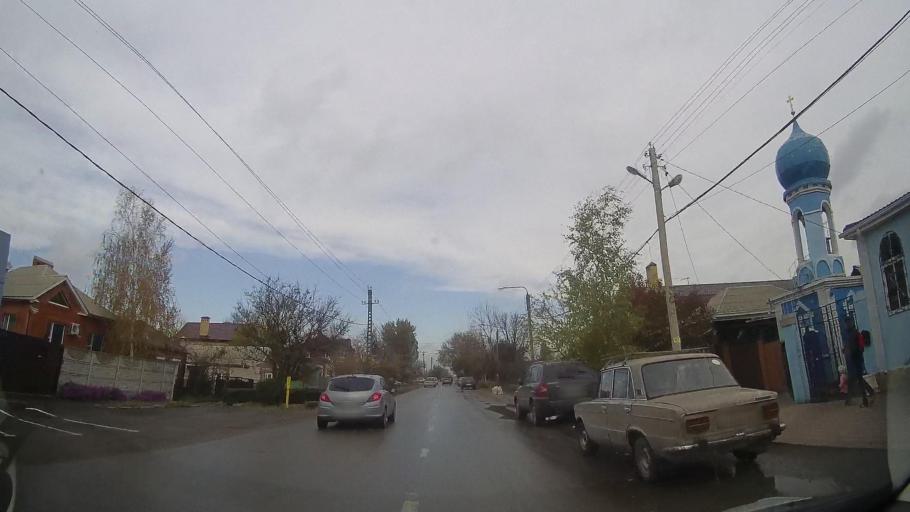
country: RU
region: Rostov
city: Bataysk
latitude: 47.1389
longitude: 39.7674
